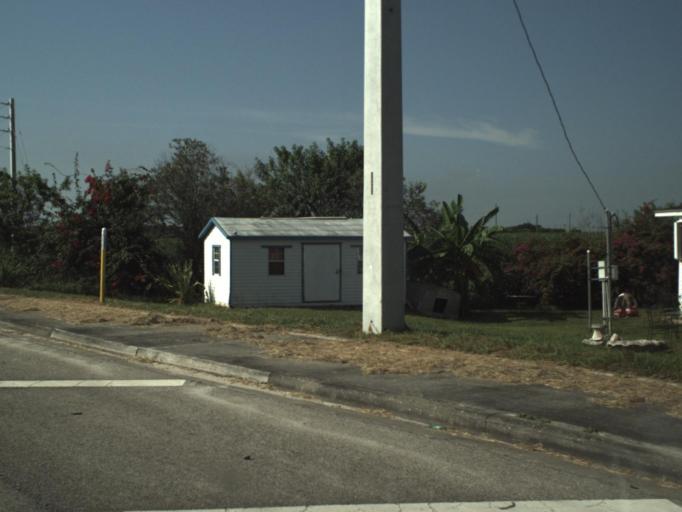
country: US
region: Florida
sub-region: Palm Beach County
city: South Bay
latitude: 26.6608
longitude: -80.7144
